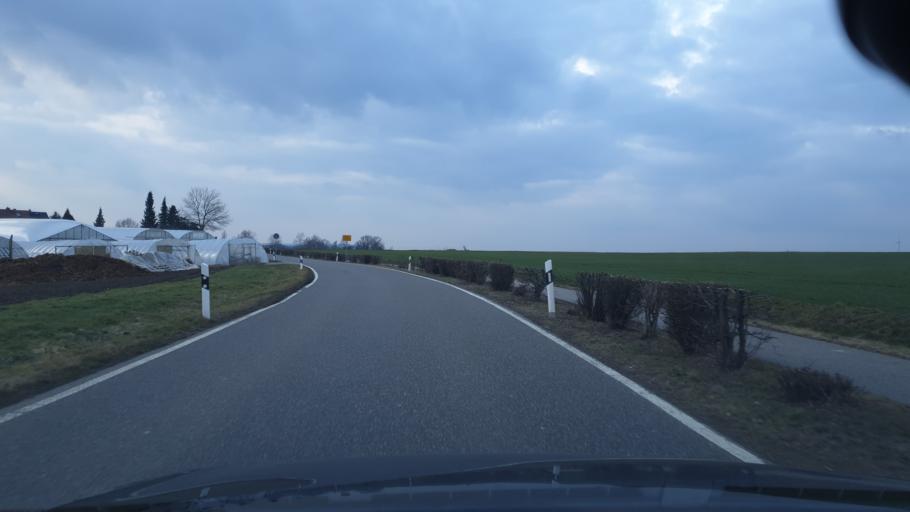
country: DE
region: Saxony
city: Altmittweida
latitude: 50.9878
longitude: 12.9340
